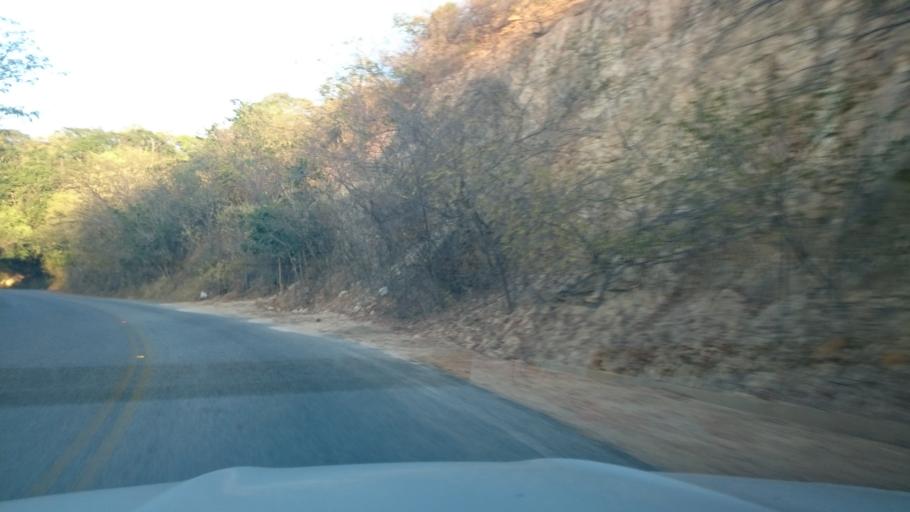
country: BR
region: Rio Grande do Norte
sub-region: Umarizal
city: Umarizal
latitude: -6.0191
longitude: -37.9906
